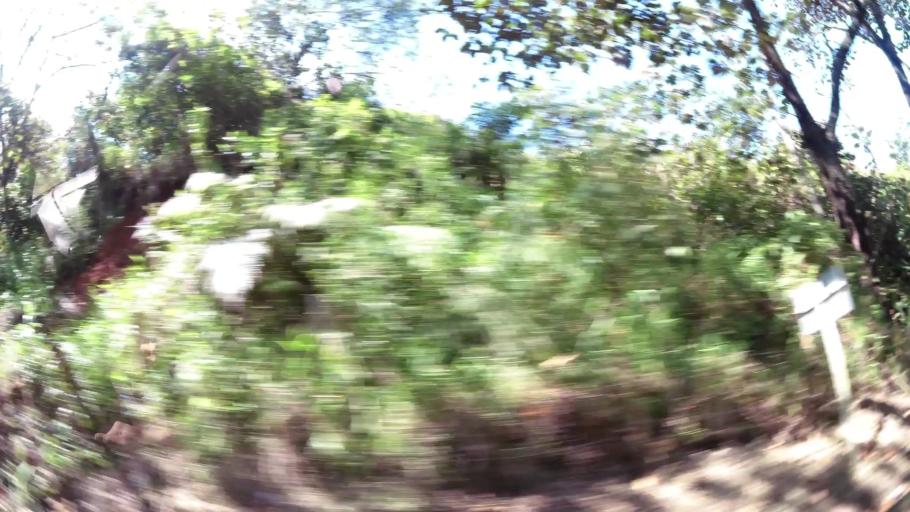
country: CO
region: Valle del Cauca
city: Cali
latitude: 3.4281
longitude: -76.5755
